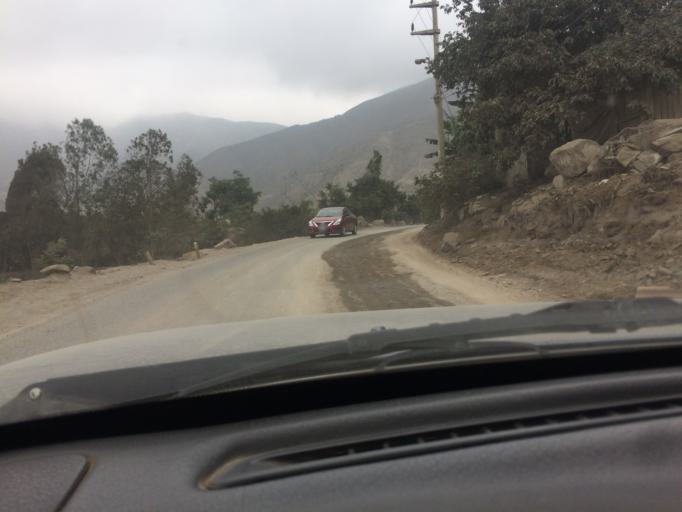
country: PE
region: Lima
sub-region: Lima
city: Cieneguilla
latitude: -12.1712
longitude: -76.8620
